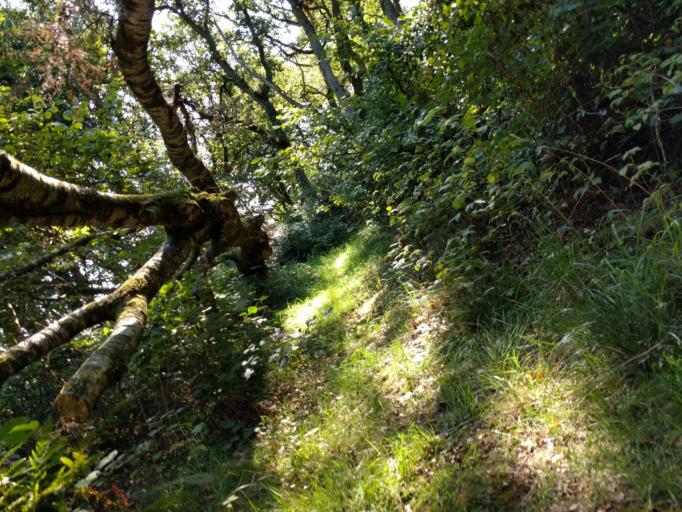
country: DK
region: Central Jutland
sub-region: Skive Kommune
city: Hojslev
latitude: 56.6646
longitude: 9.0931
